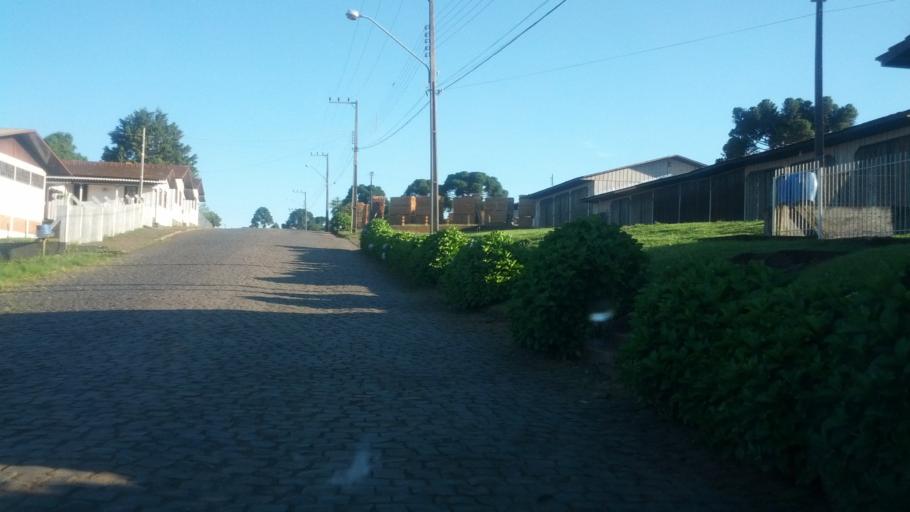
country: BR
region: Rio Grande do Sul
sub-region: Vacaria
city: Estrela
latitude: -27.9036
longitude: -50.7560
